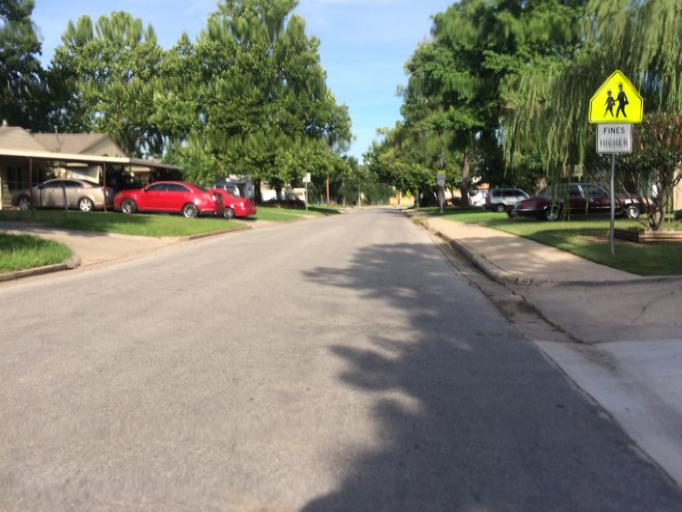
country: US
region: Oklahoma
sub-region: Cleveland County
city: Norman
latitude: 35.2244
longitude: -97.4663
